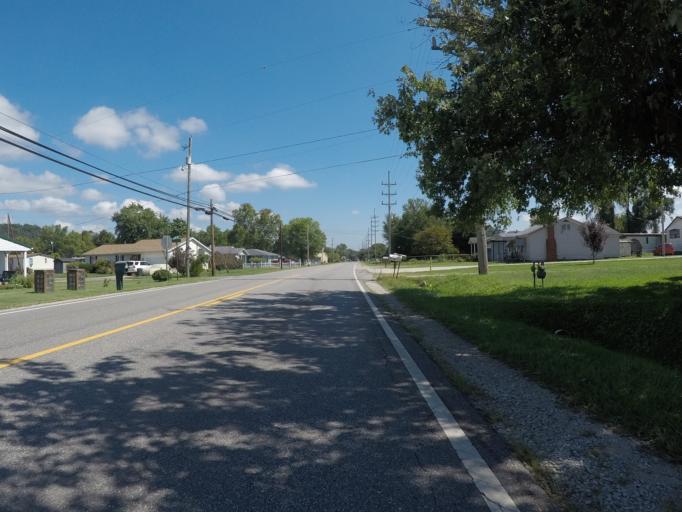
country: US
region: Ohio
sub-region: Lawrence County
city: Burlington
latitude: 38.4120
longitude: -82.5149
